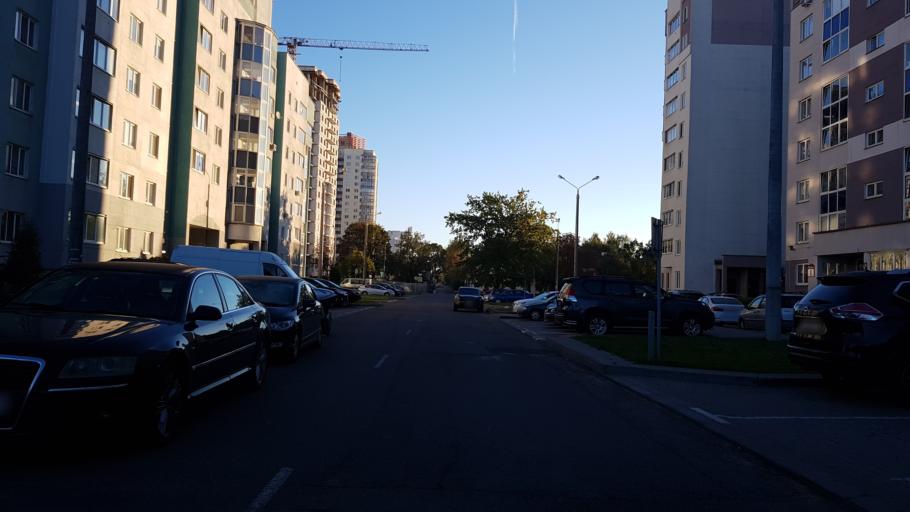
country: BY
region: Minsk
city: Minsk
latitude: 53.8811
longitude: 27.5182
